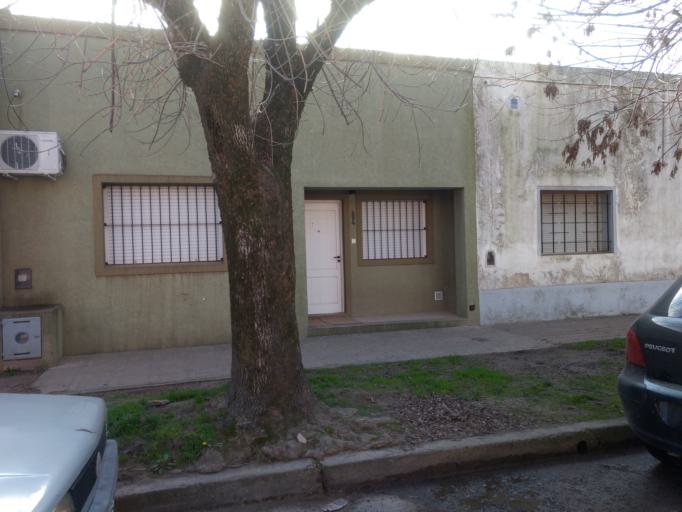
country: AR
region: Buenos Aires
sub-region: Partido de Lobos
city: Lobos
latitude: -35.1793
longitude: -59.0945
